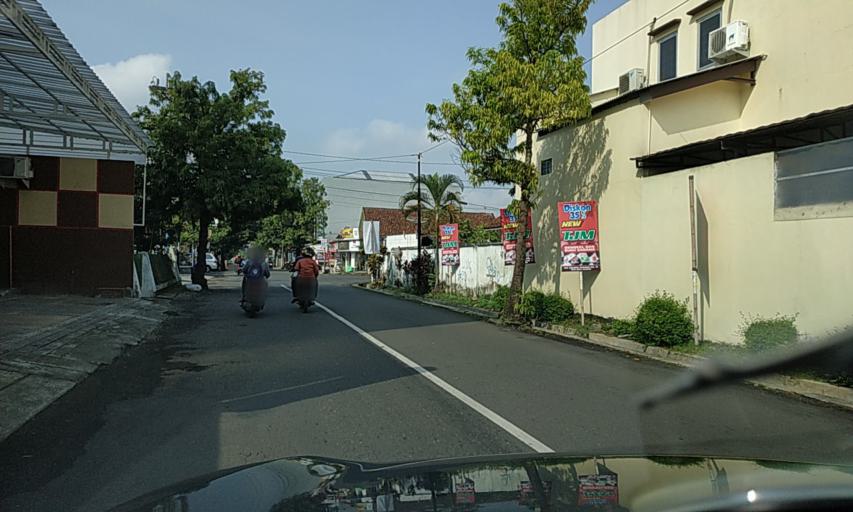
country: ID
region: Central Java
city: Purwokerto
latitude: -7.4234
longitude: 109.2410
